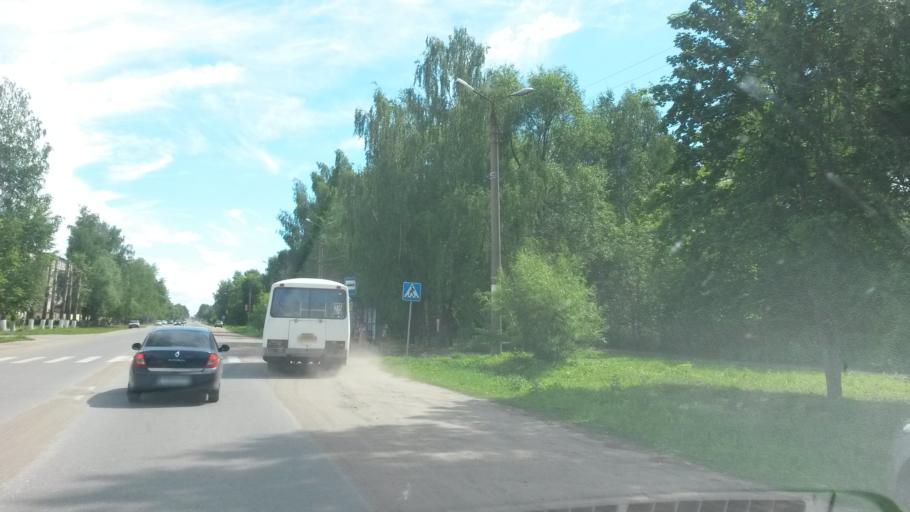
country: RU
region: Ivanovo
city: Zavolzhsk
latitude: 57.4871
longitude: 42.1421
